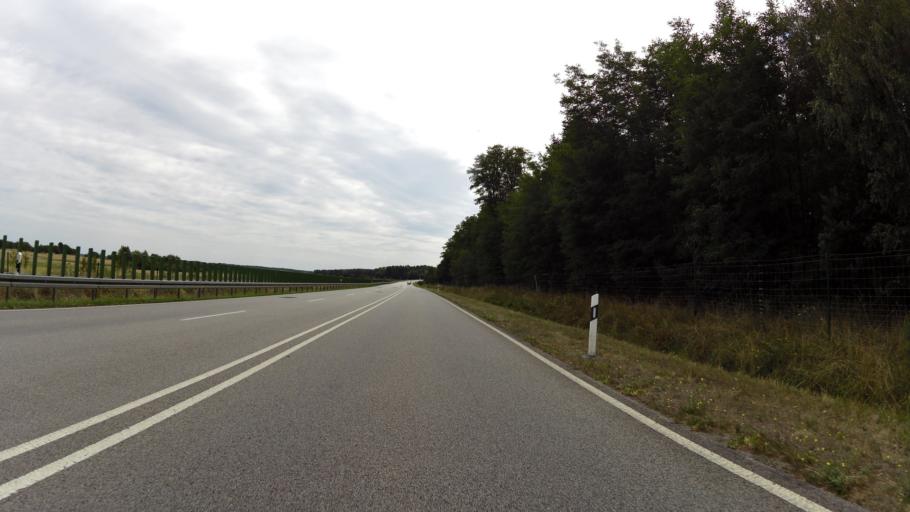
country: DE
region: Brandenburg
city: Neuzelle
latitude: 52.0474
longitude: 14.6729
